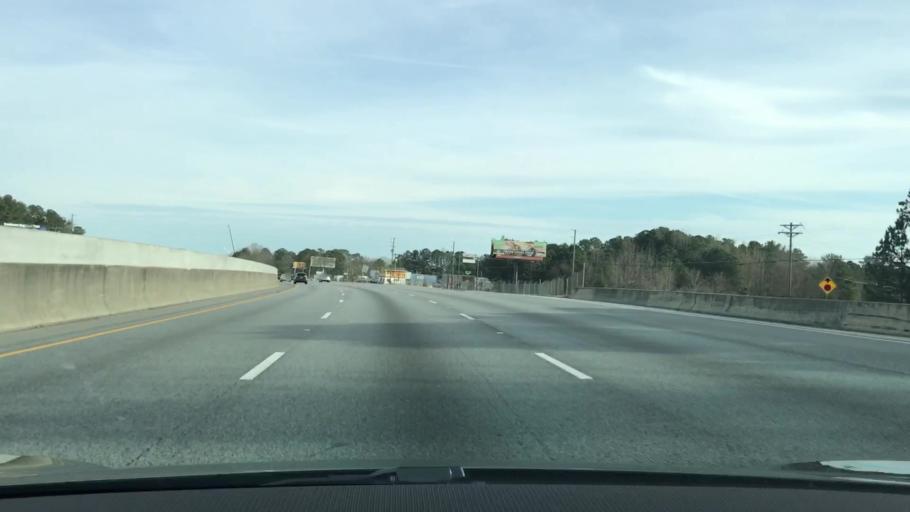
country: US
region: Georgia
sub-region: Rockdale County
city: Conyers
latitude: 33.6326
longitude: -83.9734
